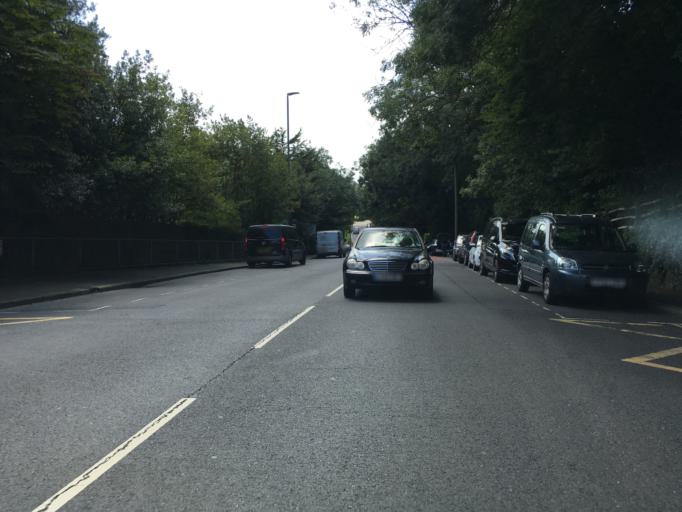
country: GB
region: England
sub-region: East Sussex
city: Hastings
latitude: 50.8631
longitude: 0.5974
